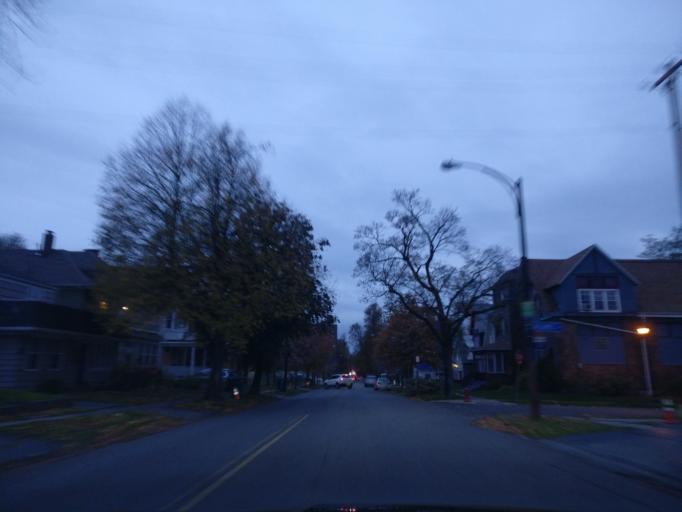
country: US
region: New York
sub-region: Erie County
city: Buffalo
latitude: 42.9113
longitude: -78.8725
